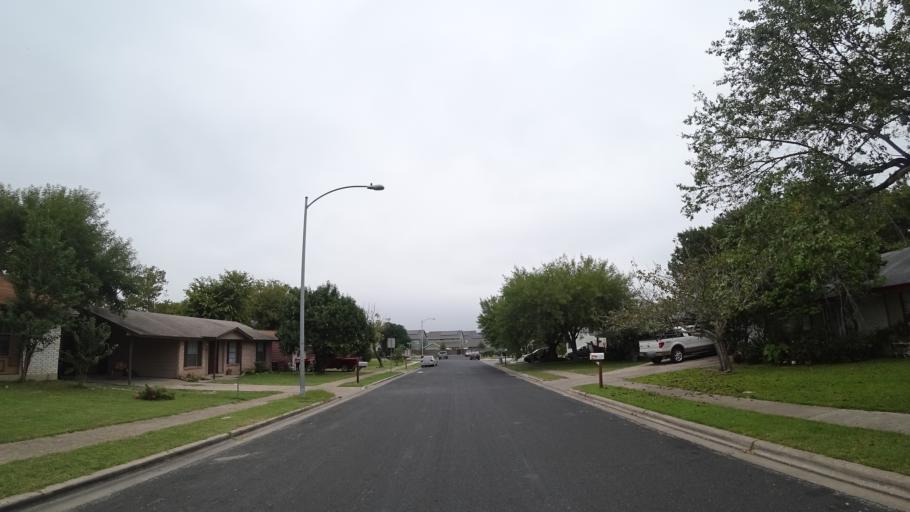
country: US
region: Texas
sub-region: Travis County
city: Onion Creek
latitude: 30.2046
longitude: -97.7777
